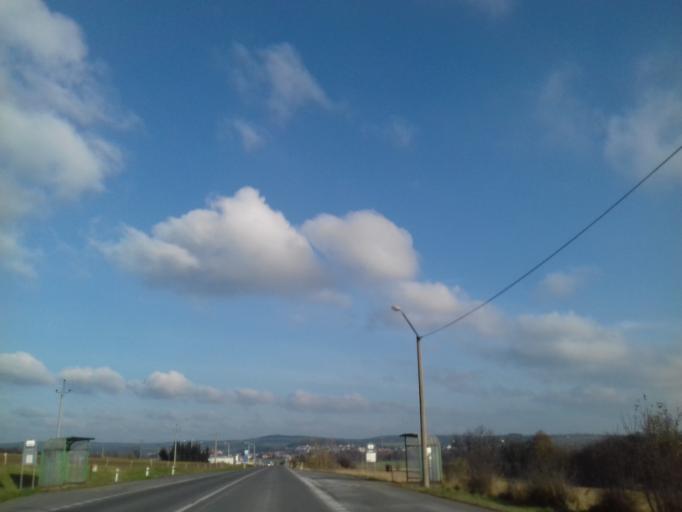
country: CZ
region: Plzensky
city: Stankov
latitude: 49.5441
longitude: 13.0414
